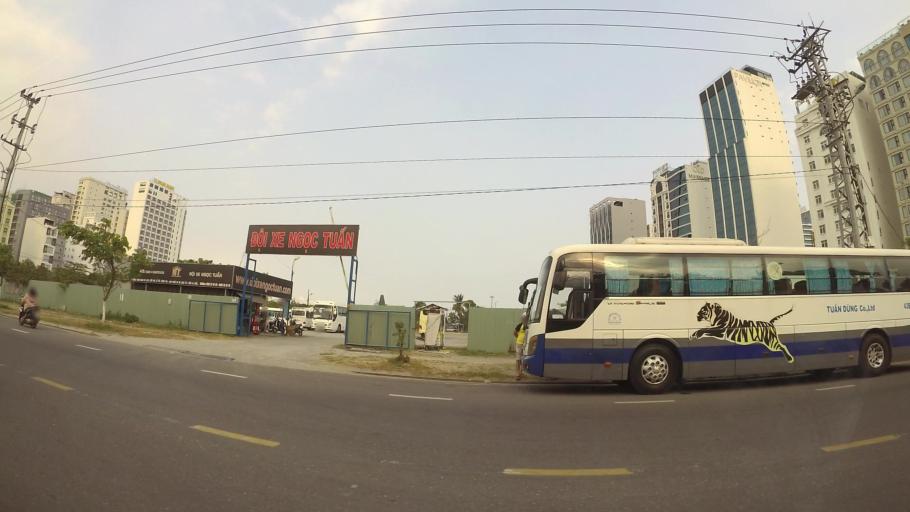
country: VN
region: Da Nang
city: Son Tra
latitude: 16.0638
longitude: 108.2432
